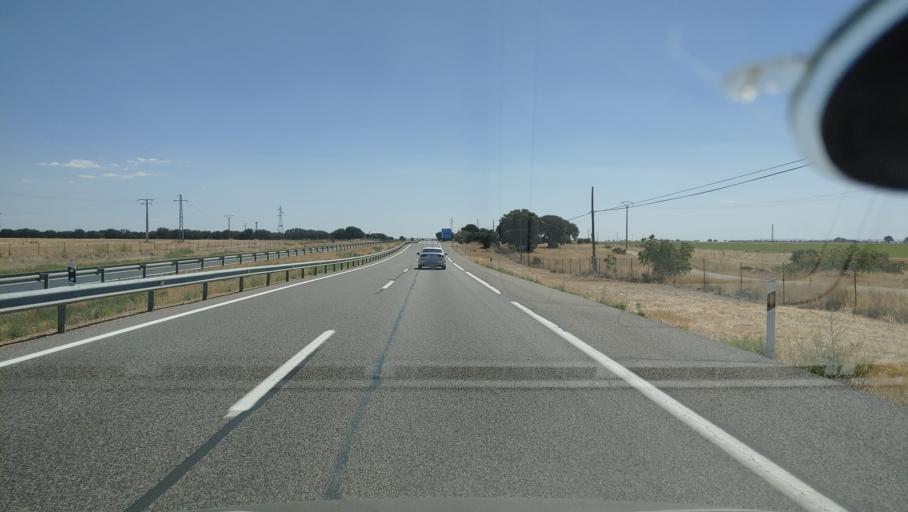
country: ES
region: Castille-La Mancha
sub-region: Provincia de Ciudad Real
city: Villarta de San Juan
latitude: 39.1939
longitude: -3.4033
